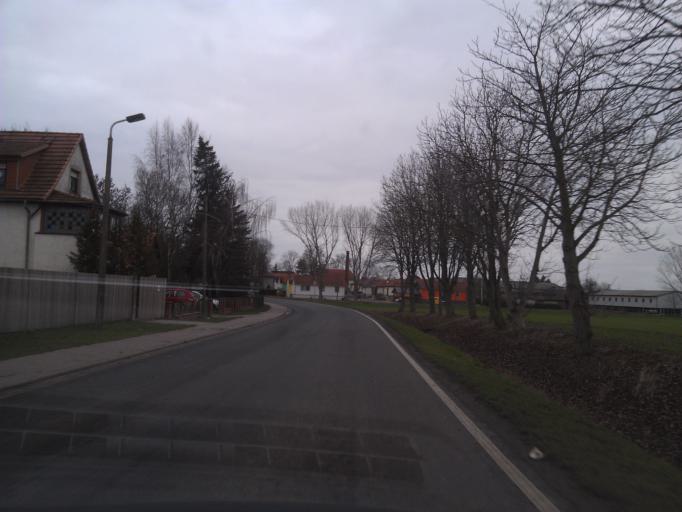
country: DE
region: Thuringia
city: Bufleben
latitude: 51.0028
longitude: 10.7367
